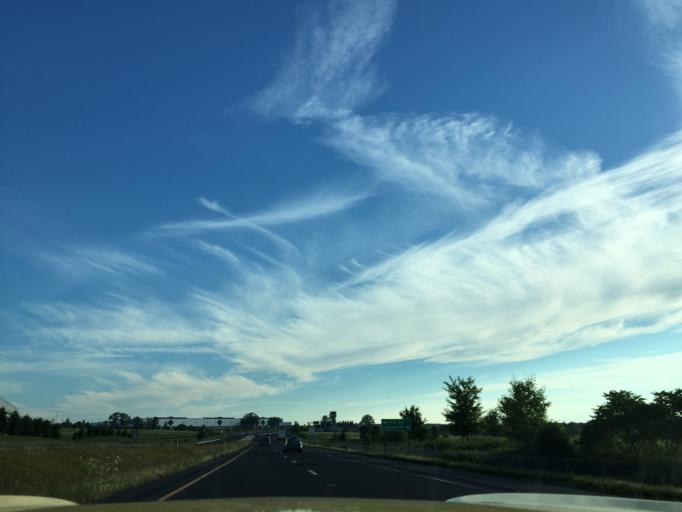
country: US
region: Pennsylvania
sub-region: Lehigh County
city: Breinigsville
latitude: 40.5470
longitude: -75.6215
